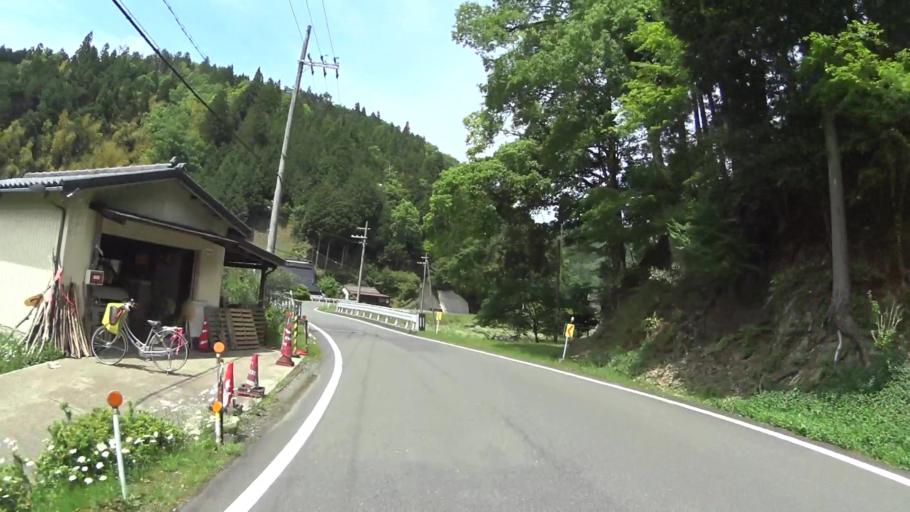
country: JP
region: Kyoto
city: Maizuru
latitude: 35.4136
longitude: 135.4621
